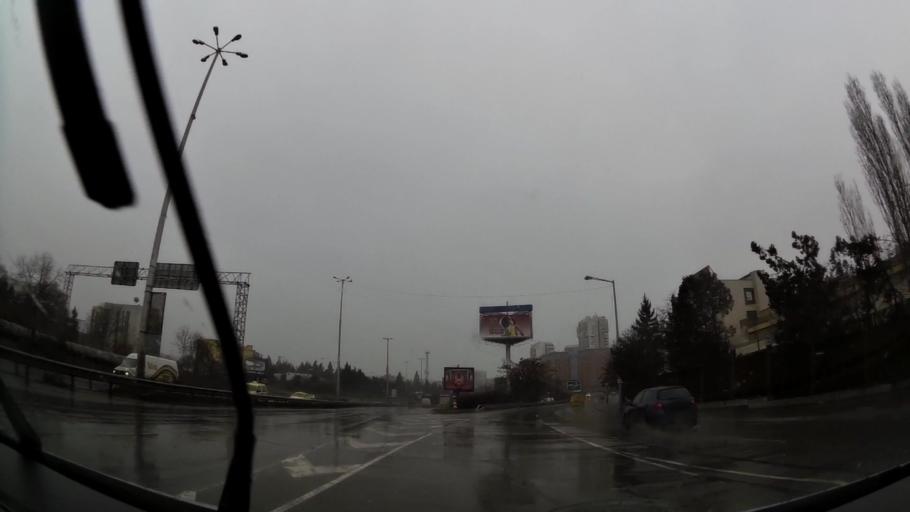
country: BG
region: Sofia-Capital
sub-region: Stolichna Obshtina
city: Sofia
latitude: 42.6584
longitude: 23.3865
